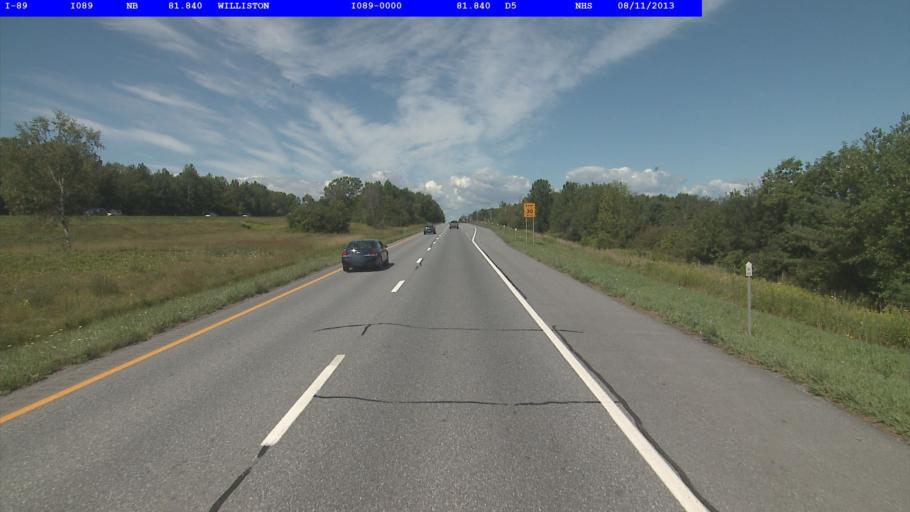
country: US
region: Vermont
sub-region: Chittenden County
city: Williston
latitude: 44.4348
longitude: -73.0727
